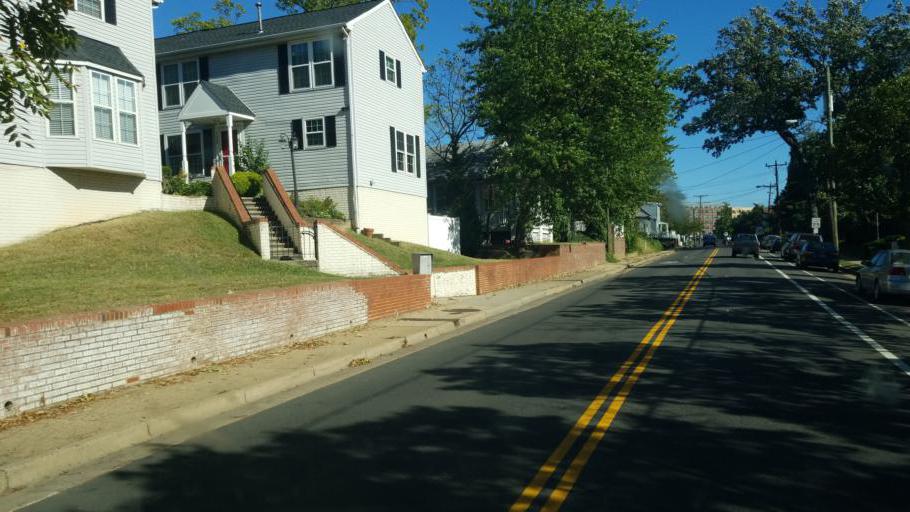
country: US
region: Virginia
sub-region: City of Alexandria
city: Alexandria
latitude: 38.8344
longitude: -77.0552
